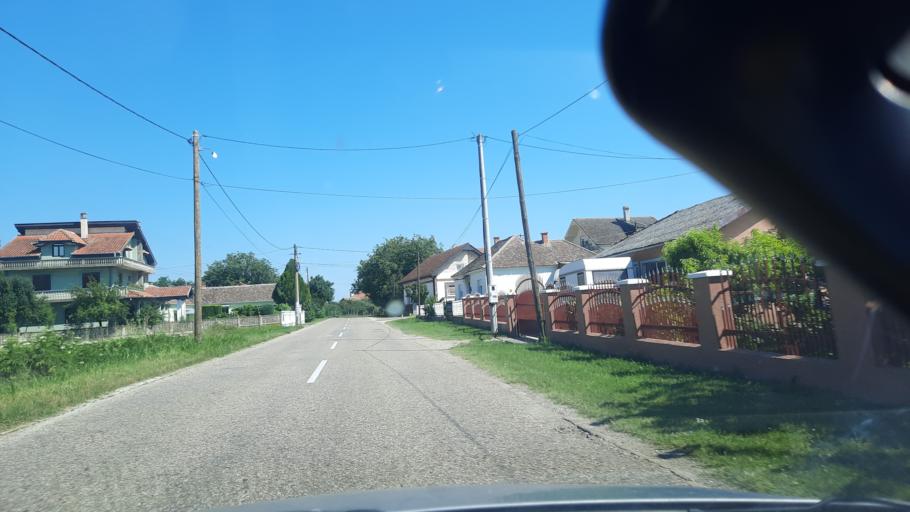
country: RS
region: Central Serbia
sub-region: Branicevski Okrug
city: Malo Crnice
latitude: 44.5913
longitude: 21.2731
